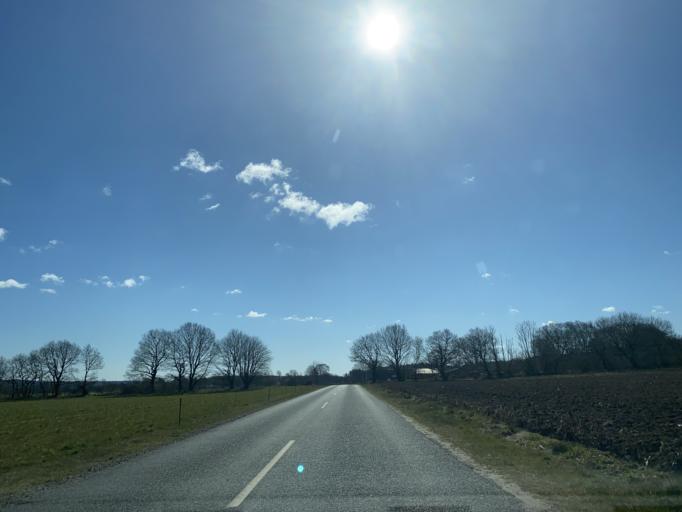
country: DK
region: Central Jutland
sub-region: Viborg Kommune
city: Bjerringbro
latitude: 56.2574
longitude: 9.6455
